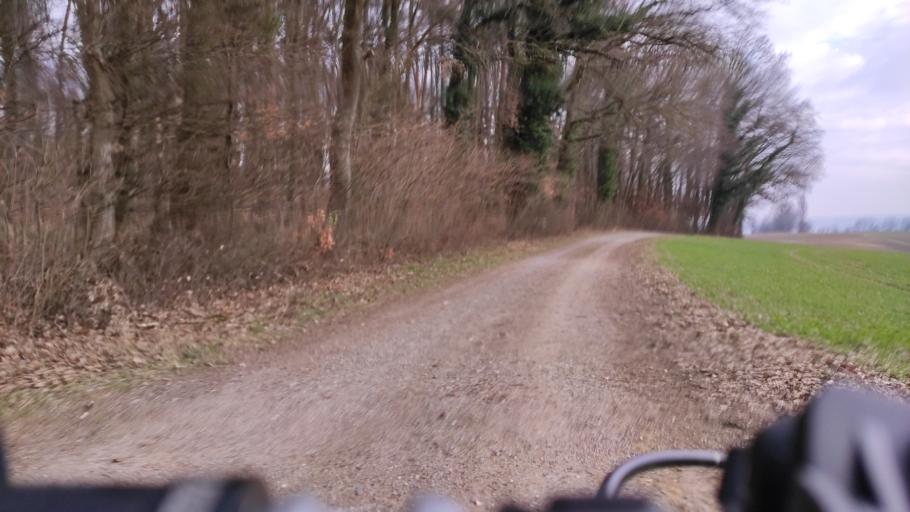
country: CH
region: Schaffhausen
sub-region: Bezirk Stein
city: Ramsen
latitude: 47.7201
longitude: 8.7990
